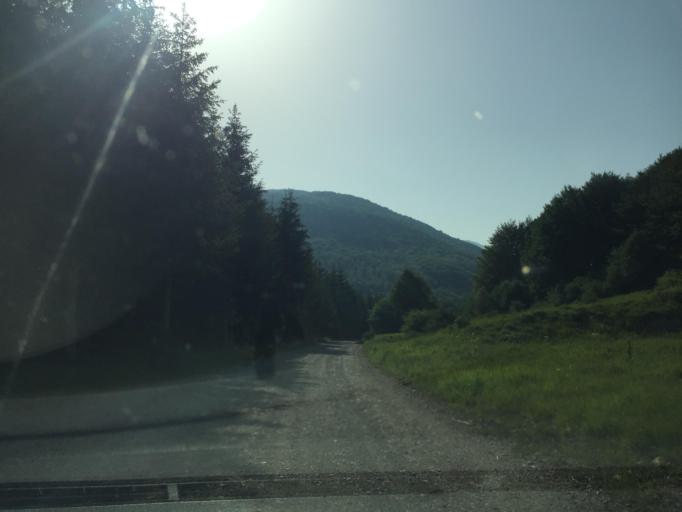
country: HR
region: Primorsko-Goranska
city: Klana
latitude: 45.4724
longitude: 14.4164
